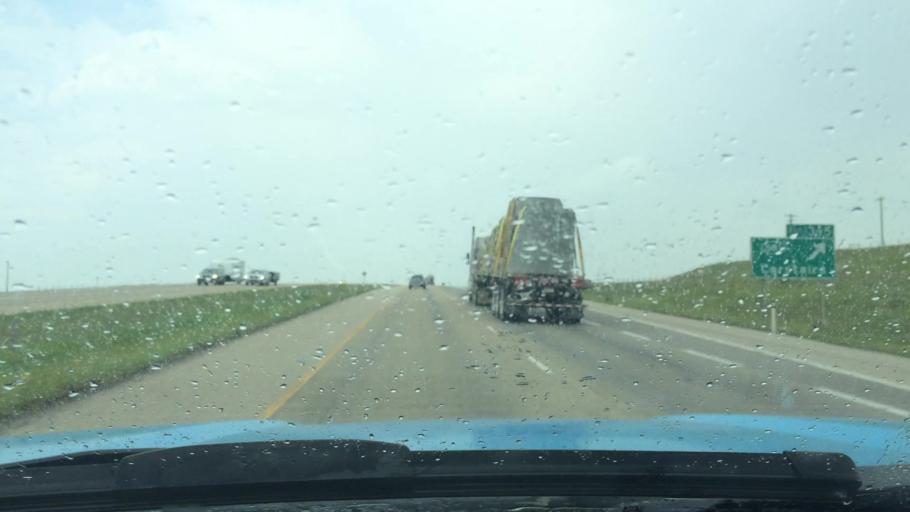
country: CA
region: Alberta
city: Carstairs
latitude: 51.5532
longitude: -114.0251
